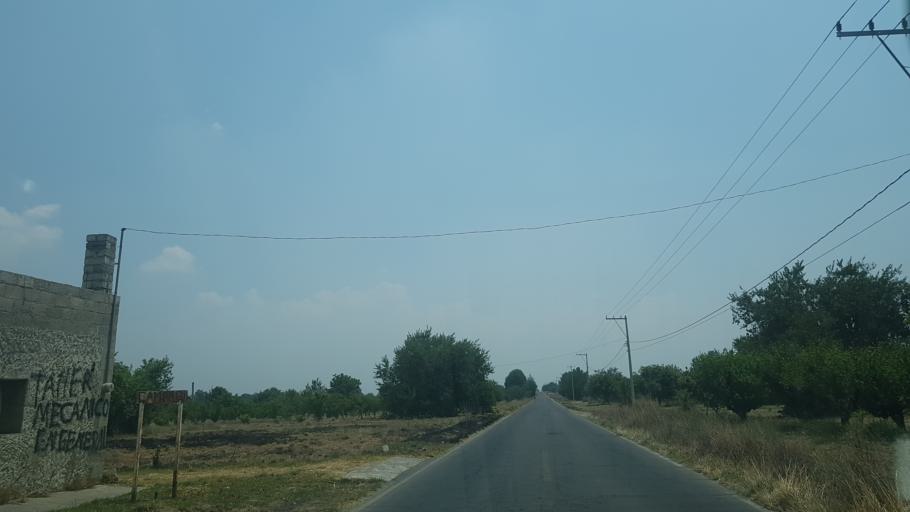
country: MX
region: Puebla
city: San Andres Calpan
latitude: 19.0990
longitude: -98.4299
